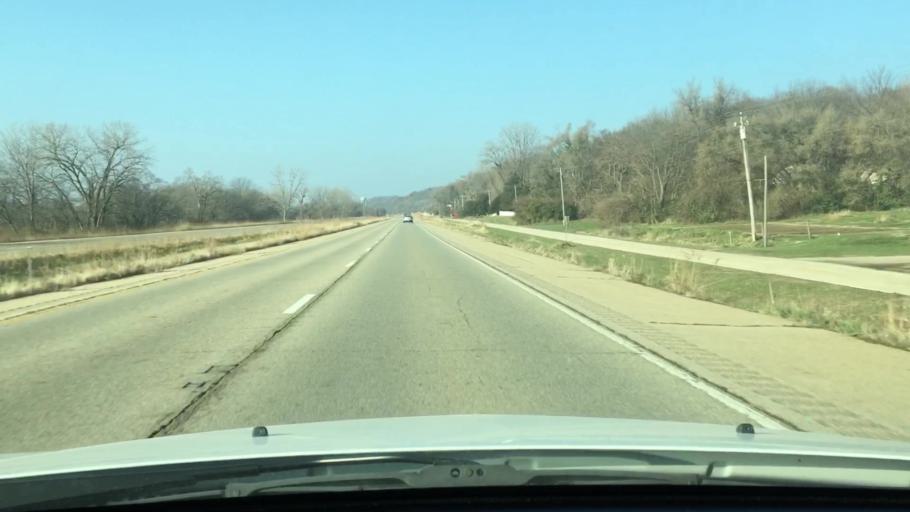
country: US
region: Illinois
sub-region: Peoria County
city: Glasford
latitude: 40.5601
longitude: -89.7605
